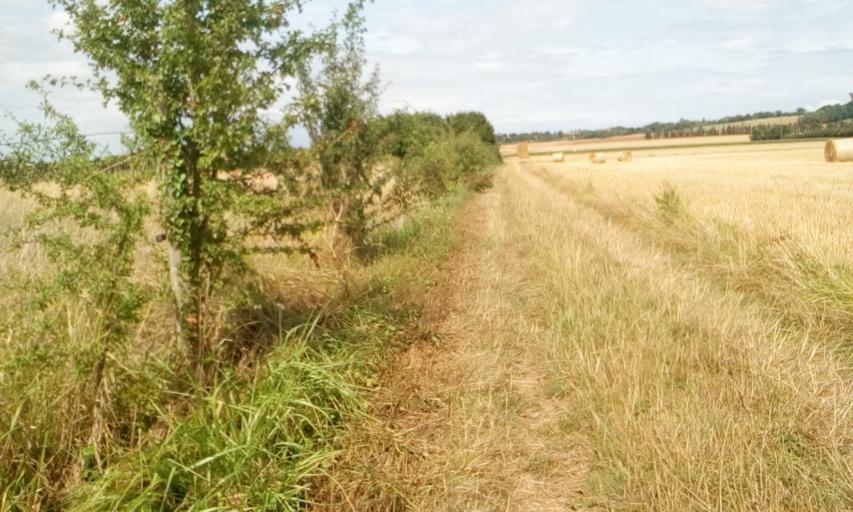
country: FR
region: Lower Normandy
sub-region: Departement du Calvados
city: Herouvillette
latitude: 49.2238
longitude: -0.2377
